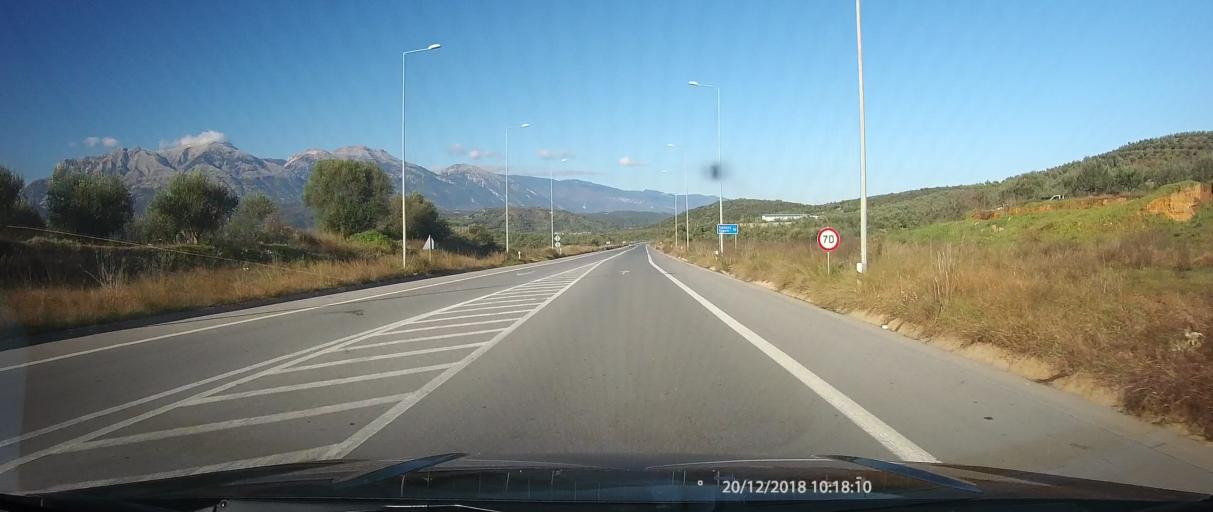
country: GR
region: Peloponnese
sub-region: Nomos Lakonias
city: Sparti
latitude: 37.1141
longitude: 22.4287
